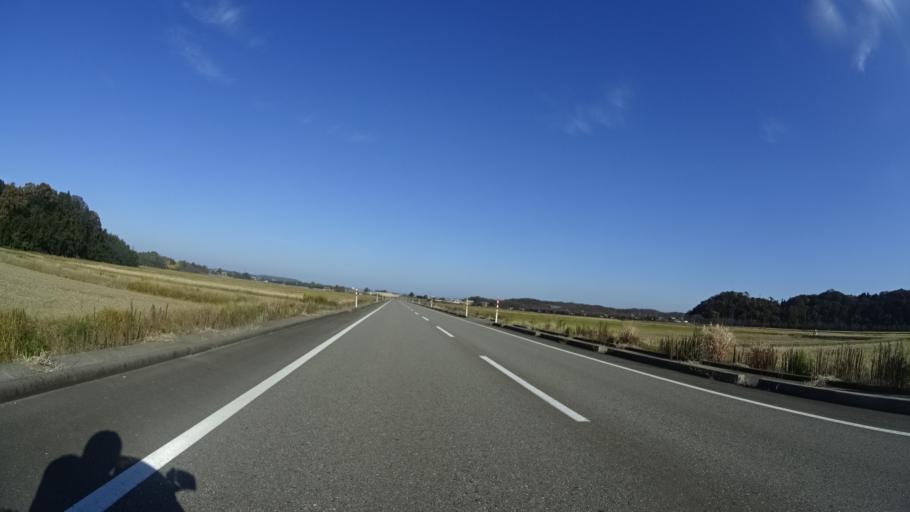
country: JP
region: Ishikawa
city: Komatsu
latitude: 36.2945
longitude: 136.3887
